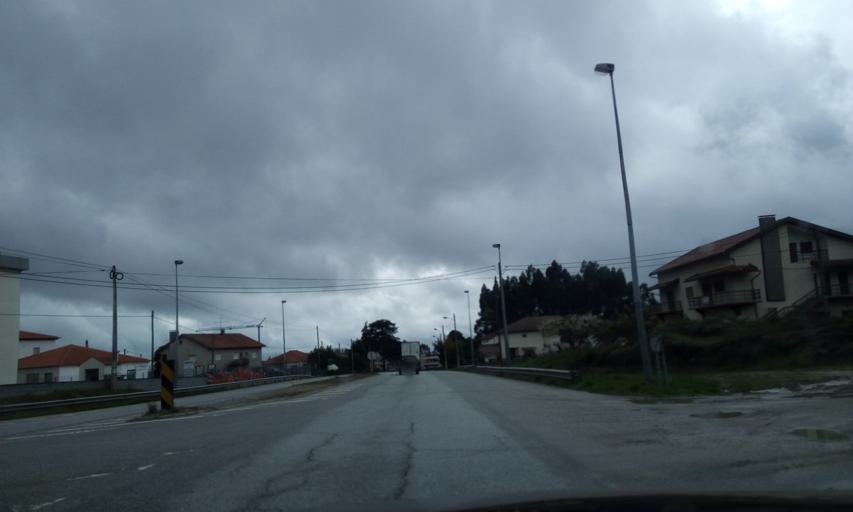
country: PT
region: Viseu
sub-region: Mangualde
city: Mangualde
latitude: 40.6052
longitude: -7.7830
